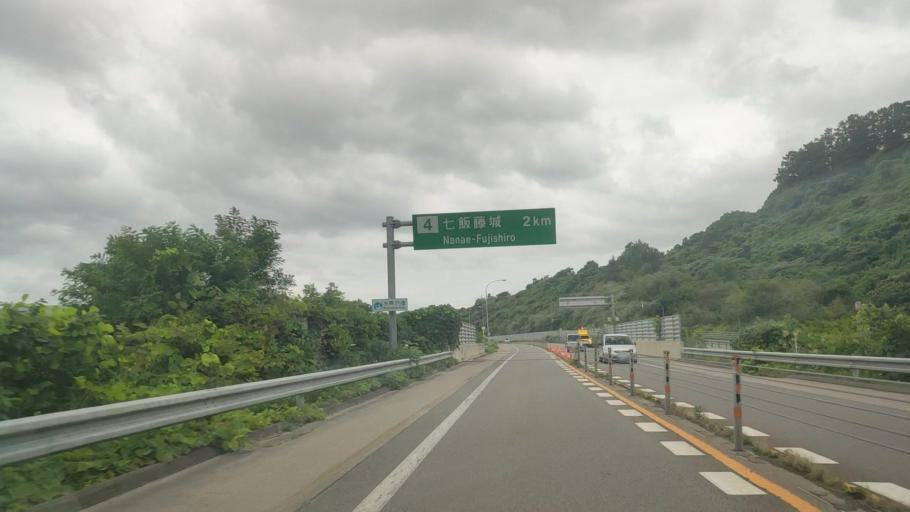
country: JP
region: Hokkaido
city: Nanae
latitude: 41.9128
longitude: 140.6915
